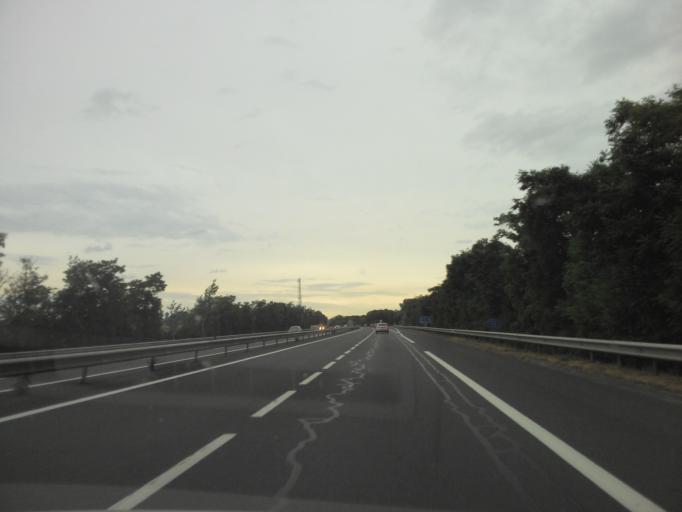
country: FR
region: Auvergne
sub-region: Departement du Puy-de-Dome
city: Riom
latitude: 45.9177
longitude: 3.1495
